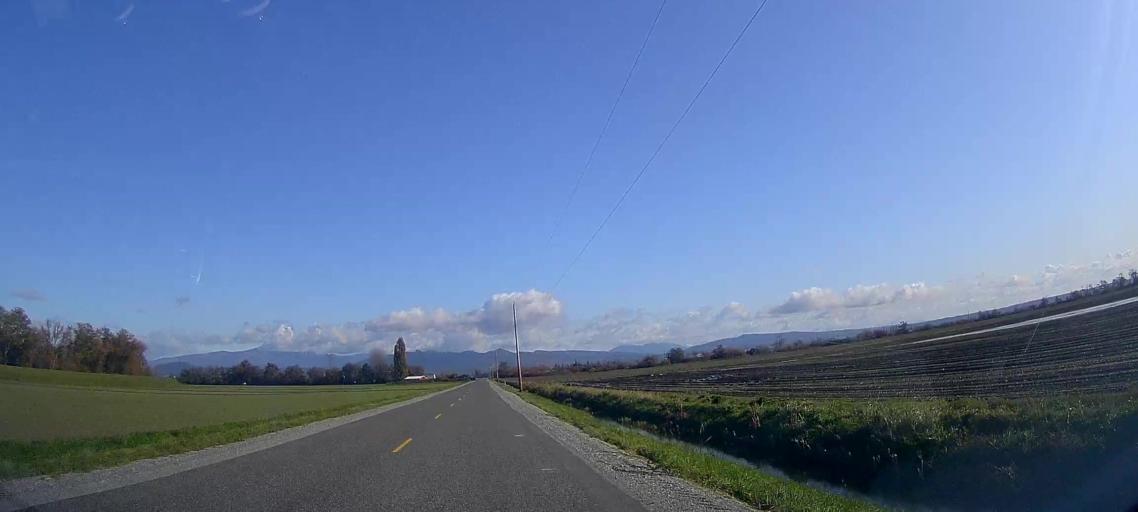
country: US
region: Washington
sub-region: Skagit County
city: Mount Vernon
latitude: 48.3556
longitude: -122.4296
